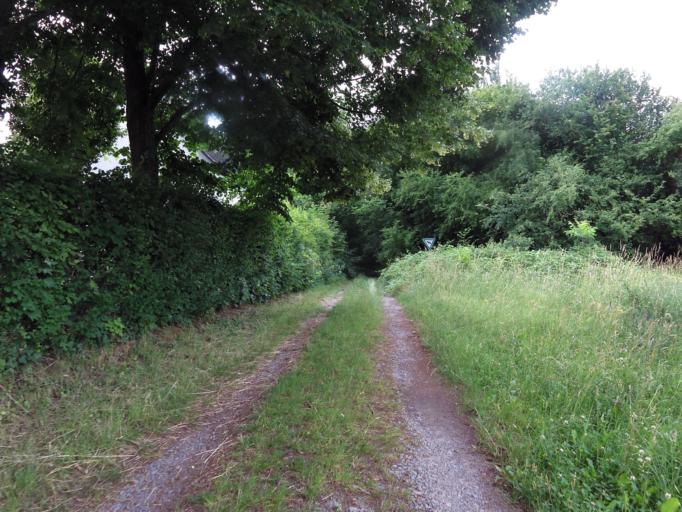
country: DE
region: Bavaria
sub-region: Regierungsbezirk Unterfranken
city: Randersacker
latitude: 49.7728
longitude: 9.9726
